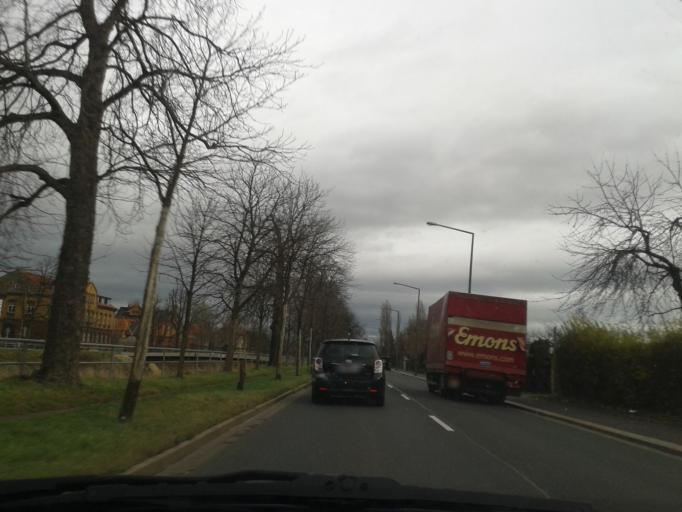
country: DE
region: Saxony
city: Dresden
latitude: 51.0526
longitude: 13.6965
